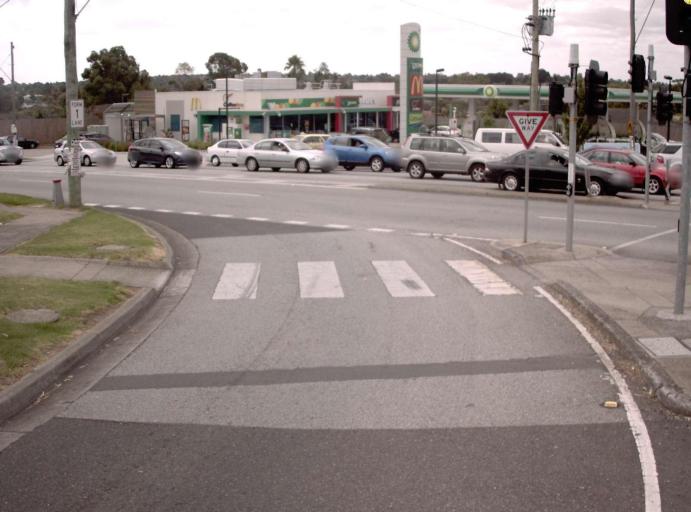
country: AU
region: Victoria
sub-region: Greater Dandenong
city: Dandenong North
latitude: -37.9712
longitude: 145.2233
